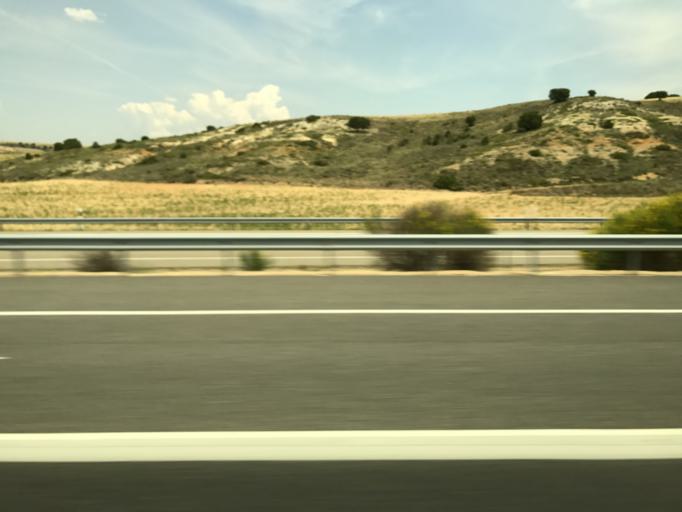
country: ES
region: Castille and Leon
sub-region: Provincia de Burgos
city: Bahabon de Esgueva
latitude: 41.8962
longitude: -3.7448
